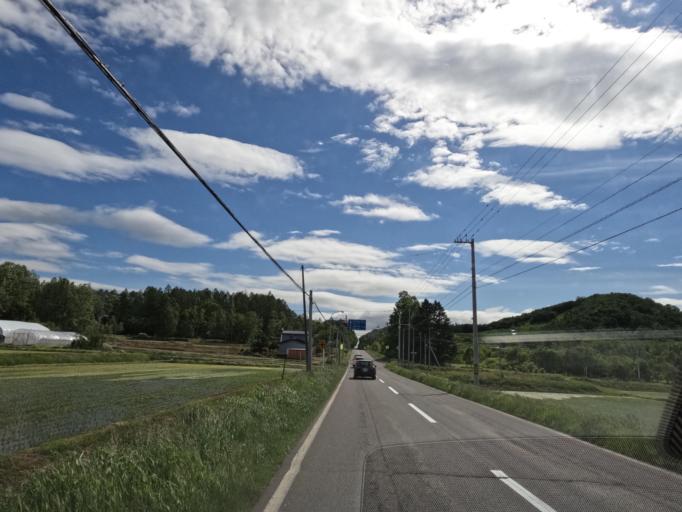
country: JP
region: Hokkaido
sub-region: Asahikawa-shi
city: Asahikawa
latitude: 43.8395
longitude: 142.5437
